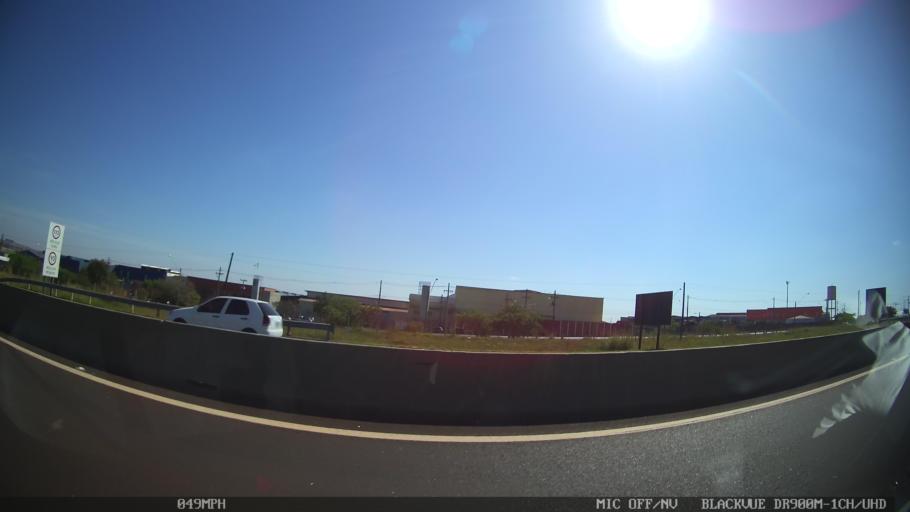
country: BR
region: Sao Paulo
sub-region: Ribeirao Preto
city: Ribeirao Preto
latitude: -21.0967
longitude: -47.7969
